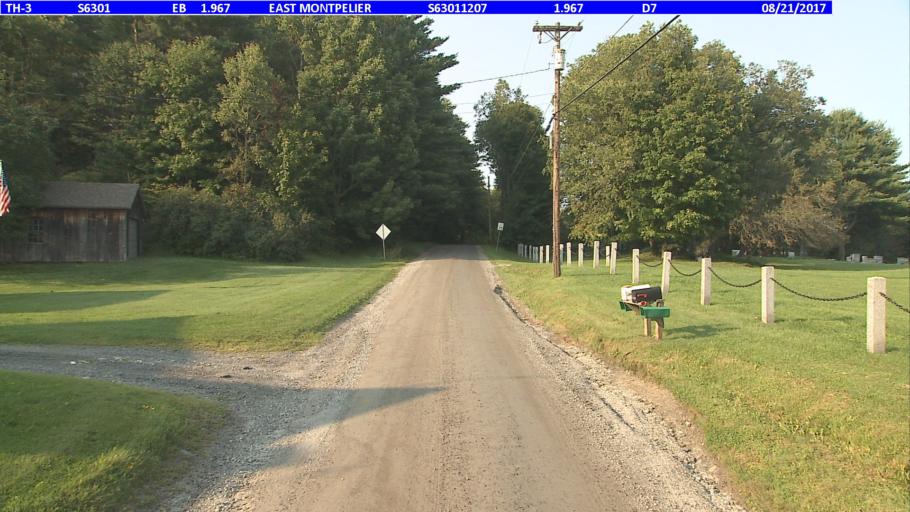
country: US
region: Vermont
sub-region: Washington County
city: Montpelier
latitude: 44.2870
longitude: -72.5212
